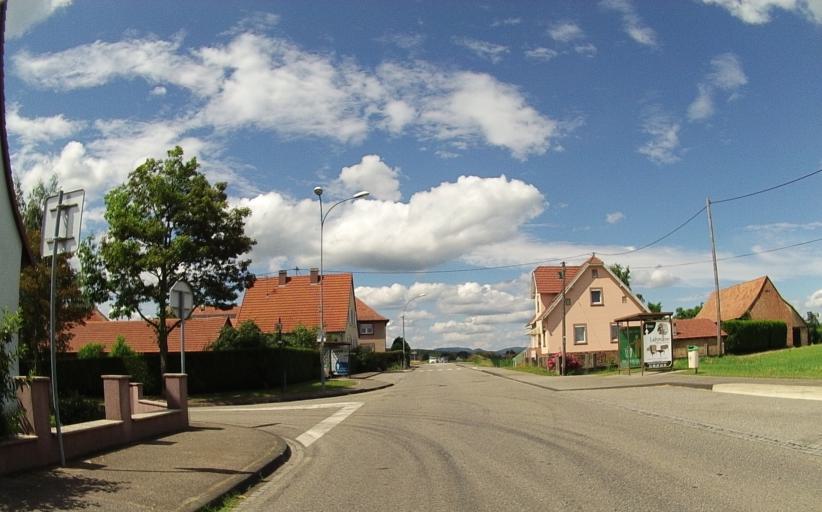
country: FR
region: Alsace
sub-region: Departement du Bas-Rhin
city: Eschbach
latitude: 48.8913
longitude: 7.7470
